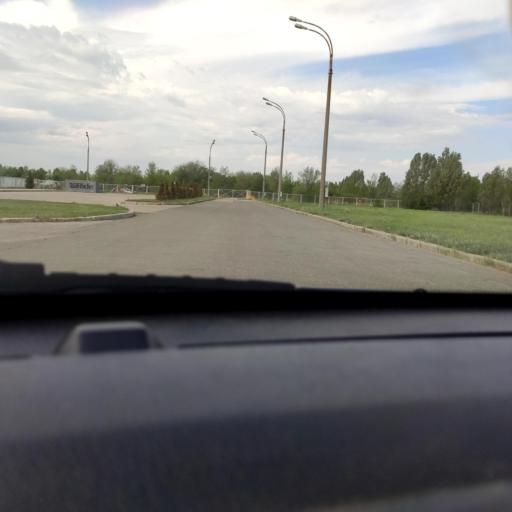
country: RU
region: Samara
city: Tol'yatti
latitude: 53.5535
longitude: 49.2491
